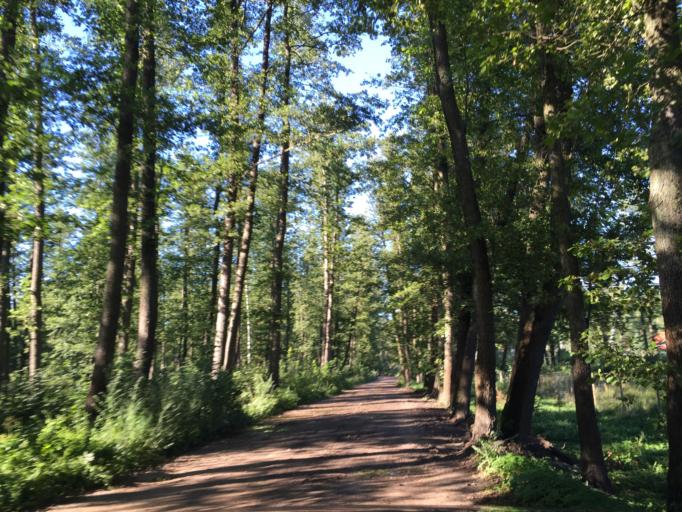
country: LV
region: Riga
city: Jaunciems
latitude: 57.0634
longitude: 24.1362
